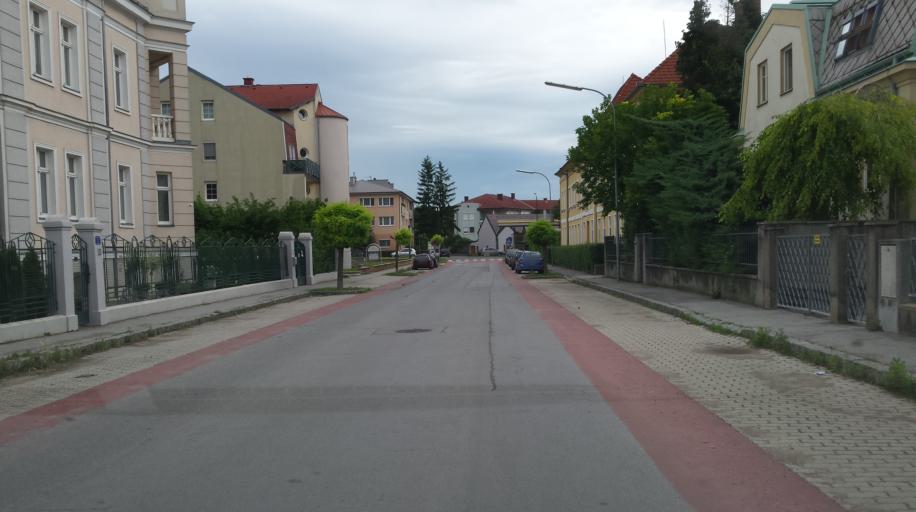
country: AT
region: Burgenland
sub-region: Politischer Bezirk Neusiedl am See
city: Bruckneudorf
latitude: 48.0206
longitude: 16.7821
